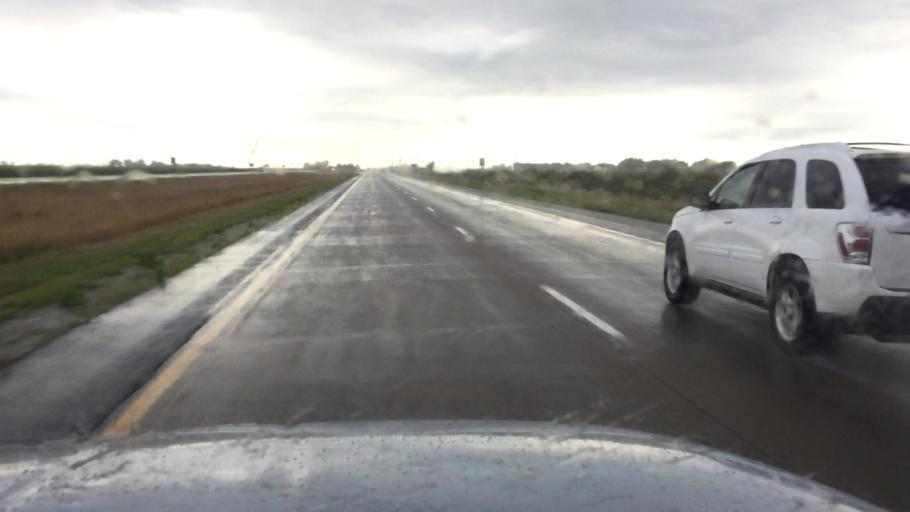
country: US
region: Iowa
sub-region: Henry County
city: Winfield
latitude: 41.1237
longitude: -91.5403
